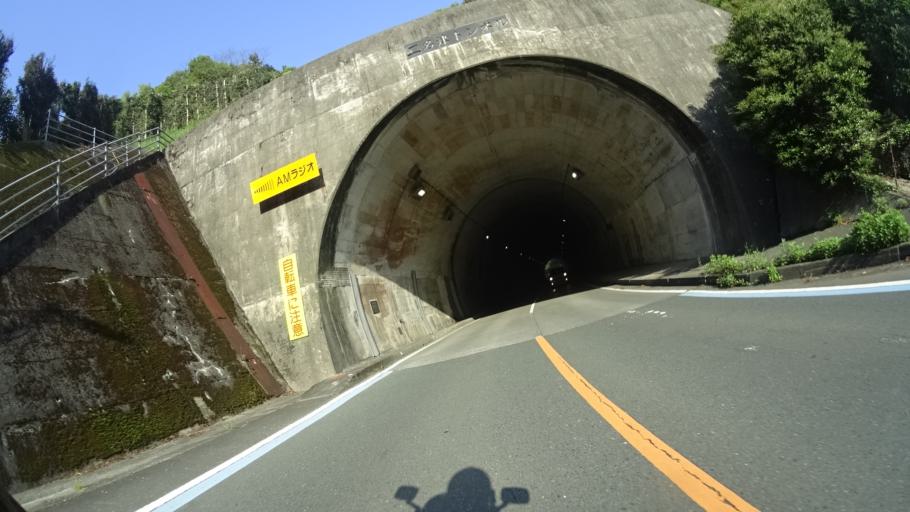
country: JP
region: Ehime
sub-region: Nishiuwa-gun
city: Ikata-cho
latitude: 33.3950
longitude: 132.1414
